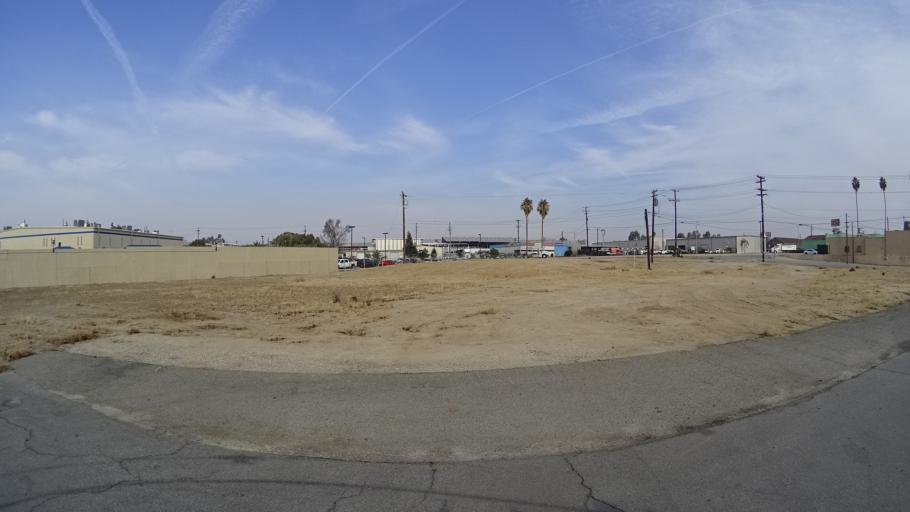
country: US
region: California
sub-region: Kern County
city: Bakersfield
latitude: 35.3790
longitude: -119.0057
